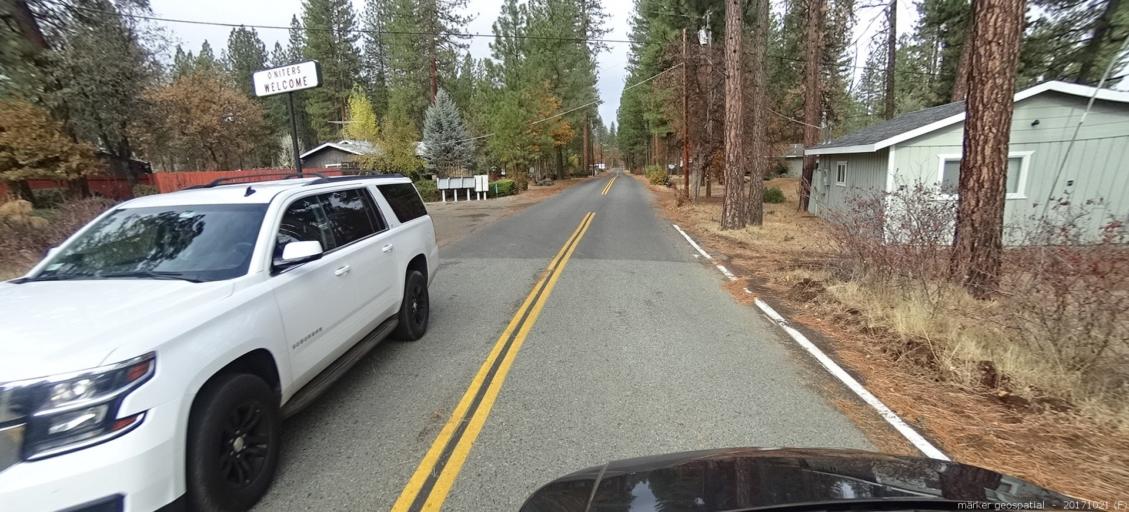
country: US
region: California
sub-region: Shasta County
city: Burney
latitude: 40.9974
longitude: -121.6302
